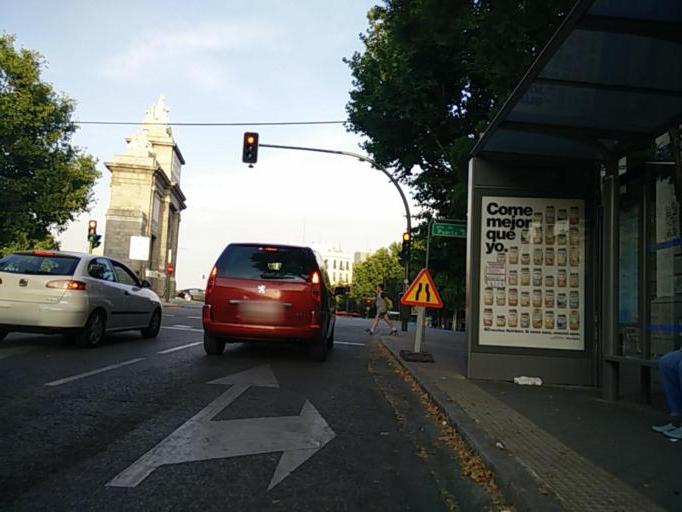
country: ES
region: Madrid
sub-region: Provincia de Madrid
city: Madrid
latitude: 40.4068
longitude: -3.7126
